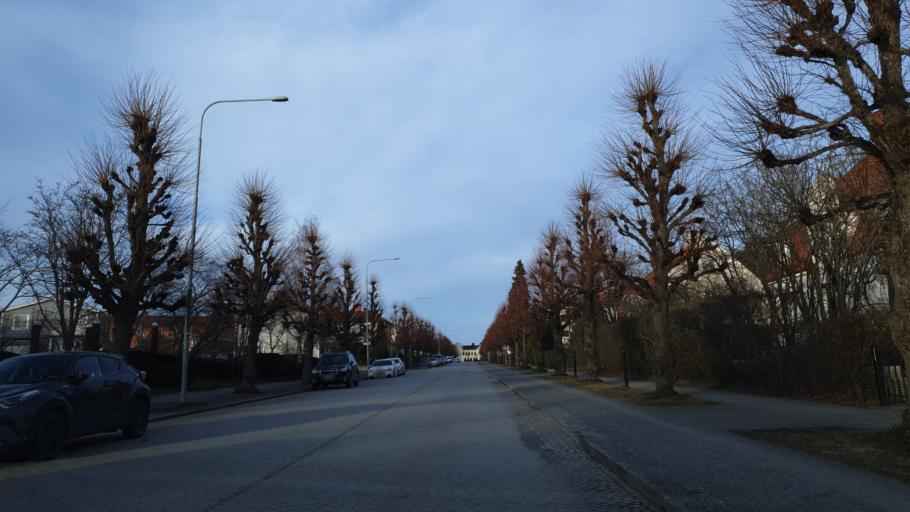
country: SE
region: Uppsala
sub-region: Enkopings Kommun
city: Enkoping
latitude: 59.6414
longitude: 17.0828
